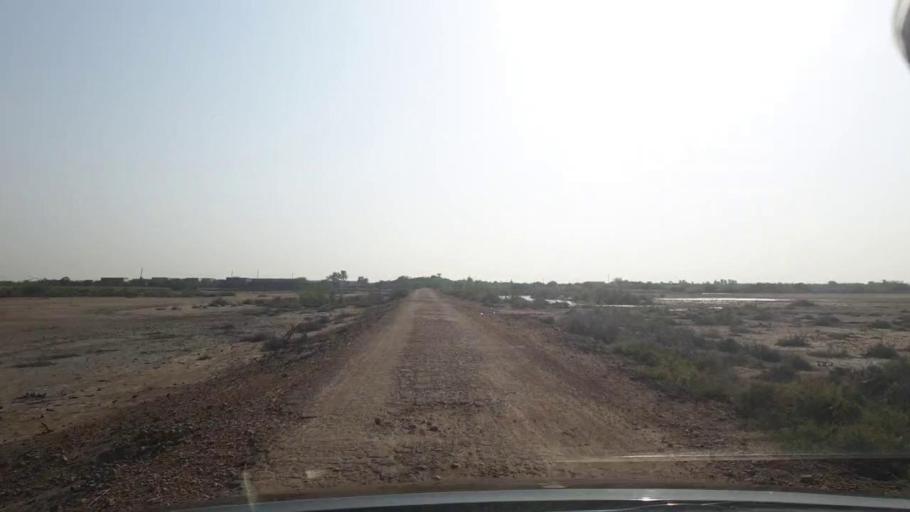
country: PK
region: Sindh
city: Tando Bago
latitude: 24.6510
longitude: 69.1346
